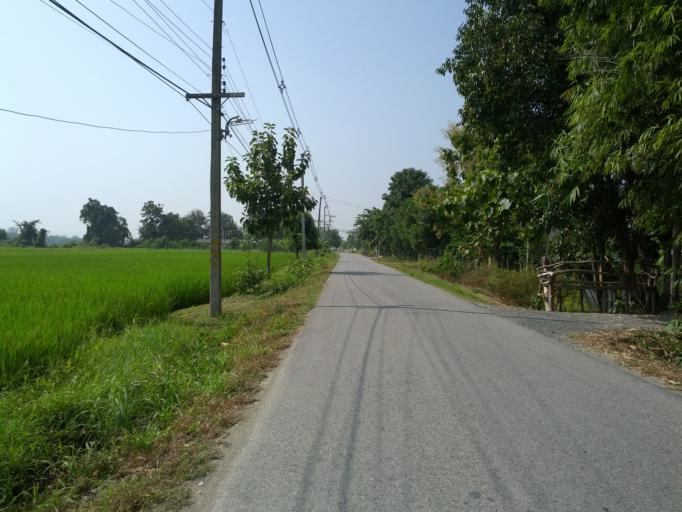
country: TH
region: Chiang Mai
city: San Kamphaeng
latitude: 18.7987
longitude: 99.0869
